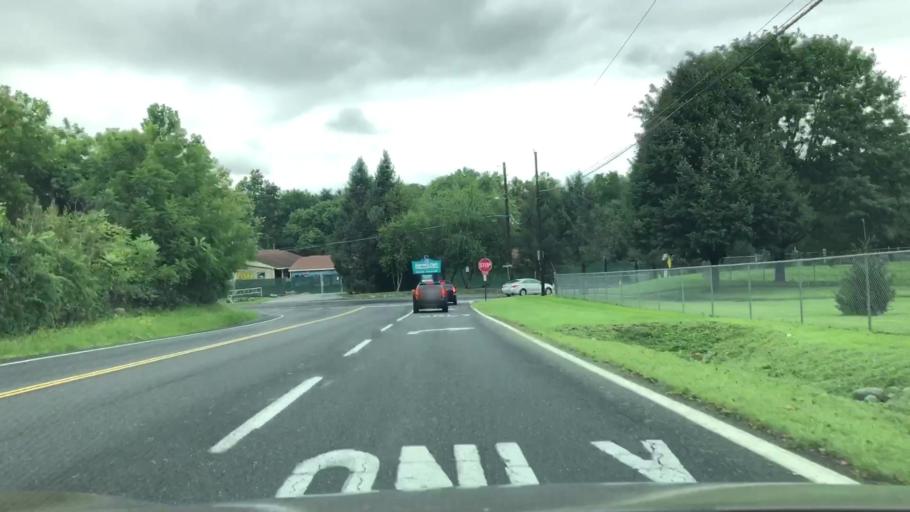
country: US
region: Pennsylvania
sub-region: Lehigh County
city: Dorneyville
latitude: 40.5764
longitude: -75.5364
